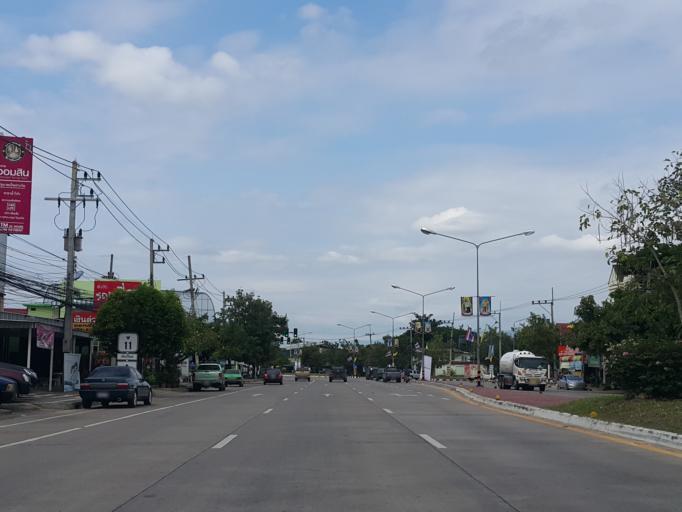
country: TH
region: Lampang
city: Lampang
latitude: 18.3096
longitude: 99.4652
